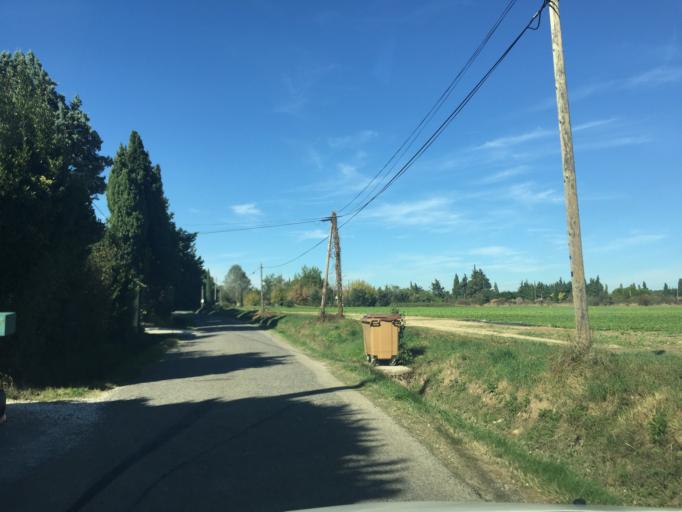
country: FR
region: Provence-Alpes-Cote d'Azur
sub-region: Departement du Vaucluse
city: Orange
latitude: 44.1437
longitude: 4.7824
